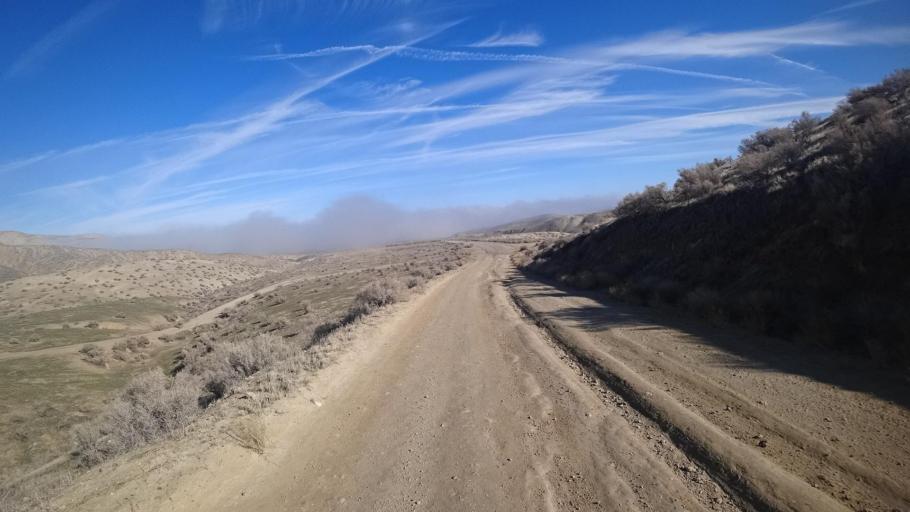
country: US
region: California
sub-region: Kern County
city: Maricopa
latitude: 35.0124
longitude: -119.4555
